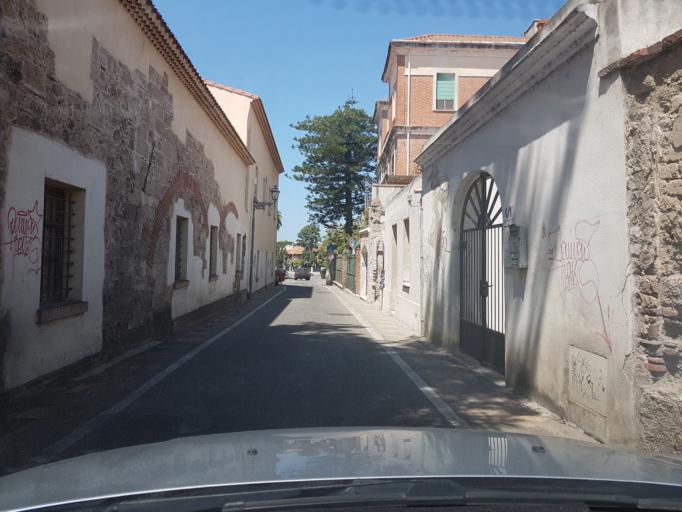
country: IT
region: Sardinia
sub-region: Provincia di Oristano
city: Oristano
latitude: 39.9041
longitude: 8.5899
